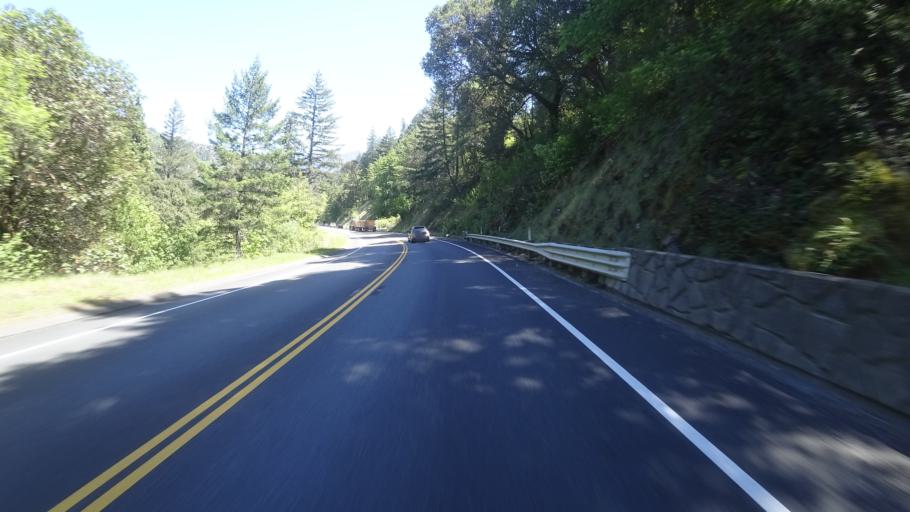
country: US
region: California
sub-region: Humboldt County
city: Willow Creek
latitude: 40.7897
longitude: -123.4509
